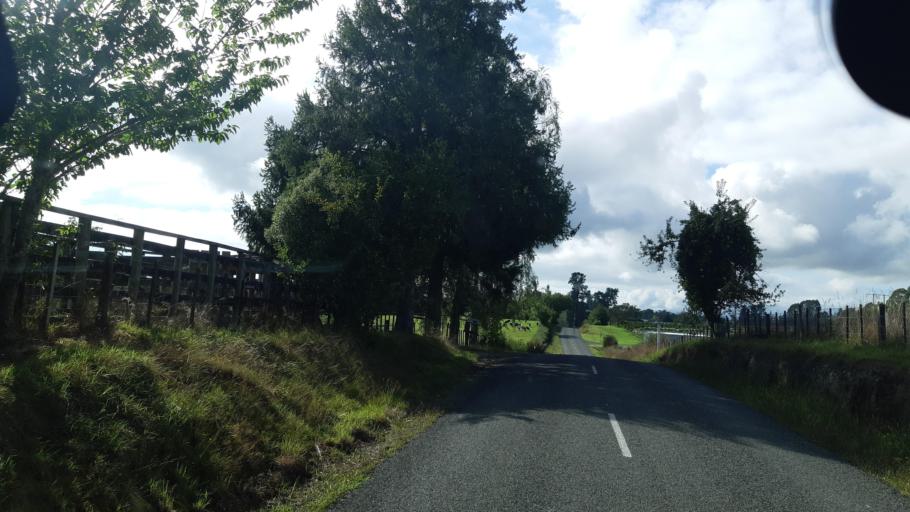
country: NZ
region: Tasman
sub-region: Tasman District
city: Mapua
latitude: -41.2582
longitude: 173.0299
